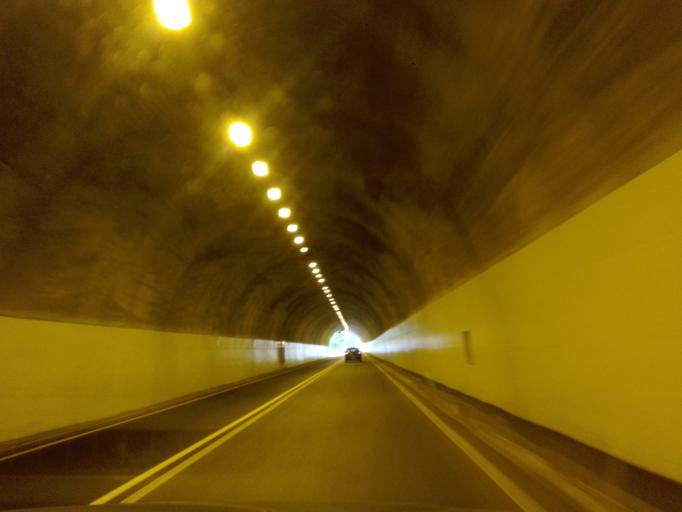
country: PT
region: Madeira
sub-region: Santana
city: Santana
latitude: 32.7564
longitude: -16.8282
